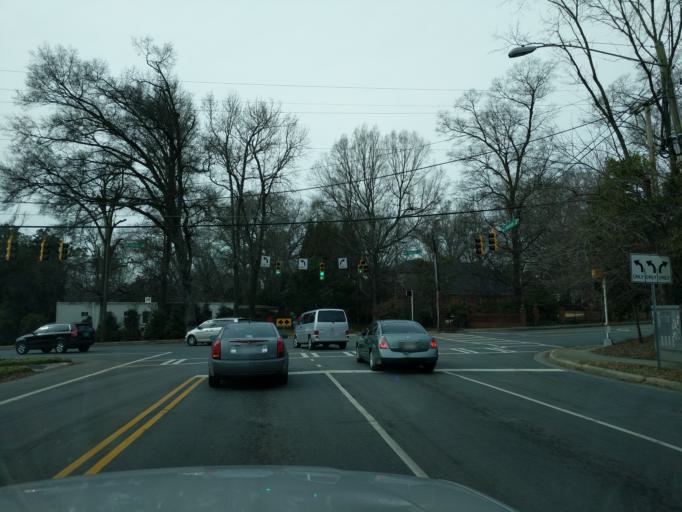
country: US
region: North Carolina
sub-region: Mecklenburg County
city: Charlotte
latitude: 35.1723
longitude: -80.8229
